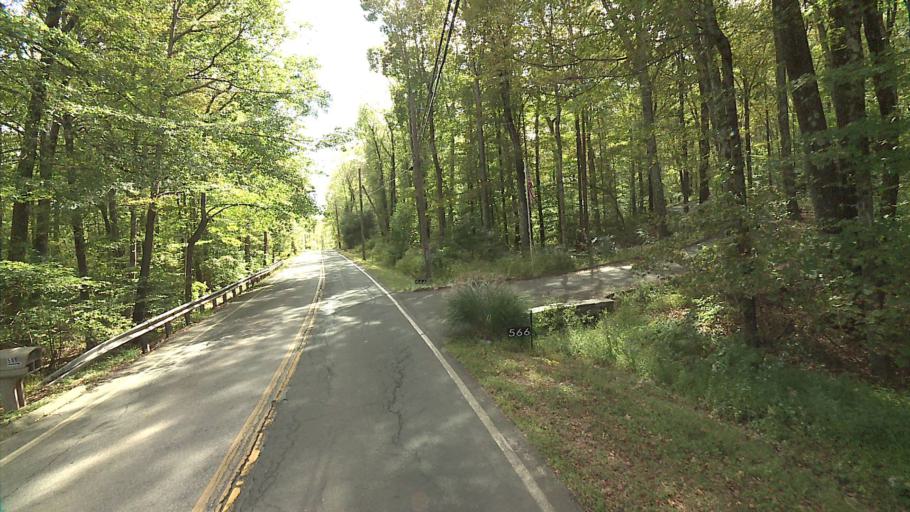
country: US
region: Connecticut
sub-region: Middlesex County
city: Higganum
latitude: 41.4057
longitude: -72.6063
